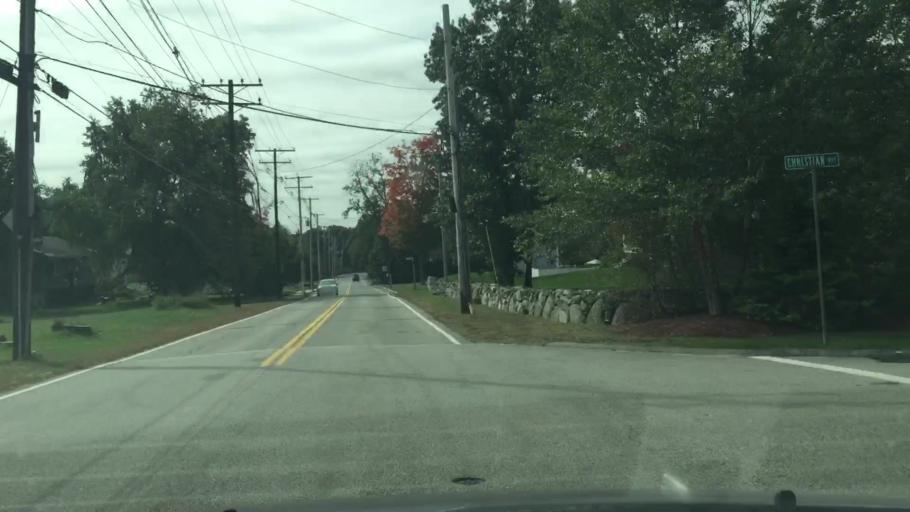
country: US
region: Massachusetts
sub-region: Middlesex County
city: Tewksbury
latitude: 42.6556
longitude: -71.2456
